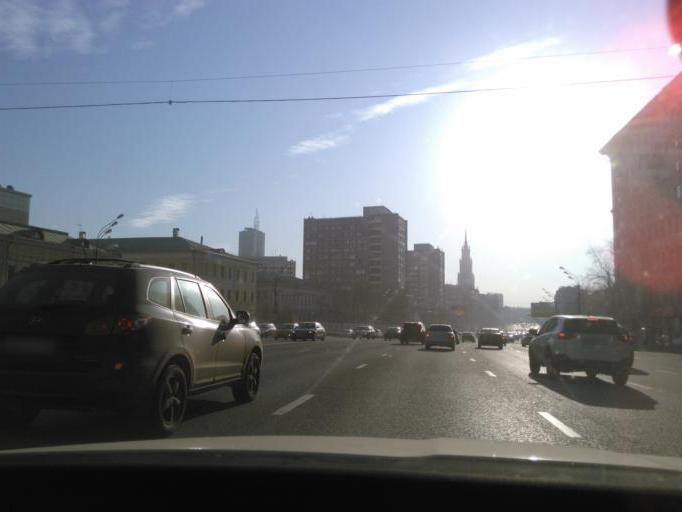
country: RU
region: Moscow
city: Moscow
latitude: 55.7721
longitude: 37.6372
